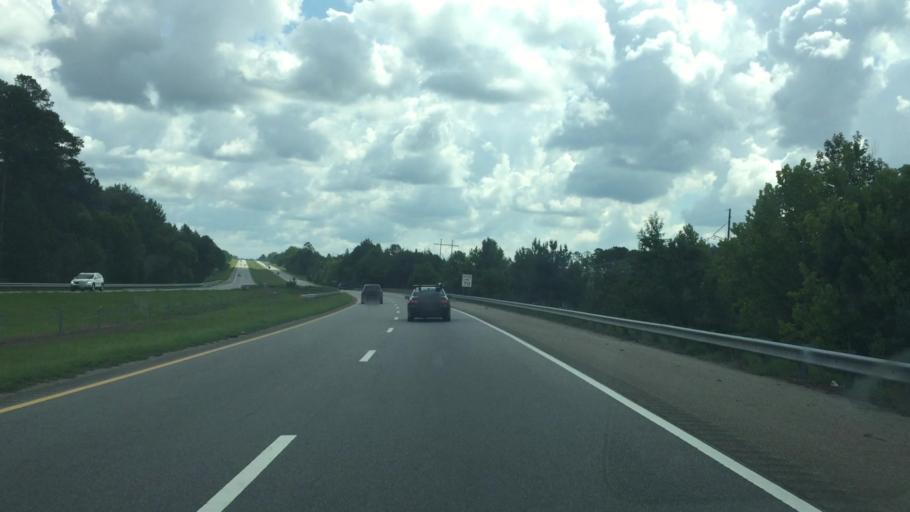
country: US
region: North Carolina
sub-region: Richmond County
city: Hamlet
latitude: 34.8522
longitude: -79.7315
